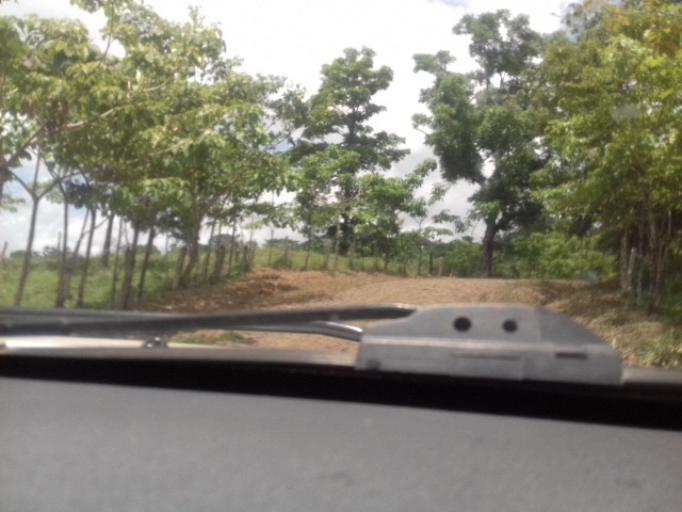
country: NI
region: Matagalpa
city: Rio Blanco
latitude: 13.0080
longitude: -85.3924
